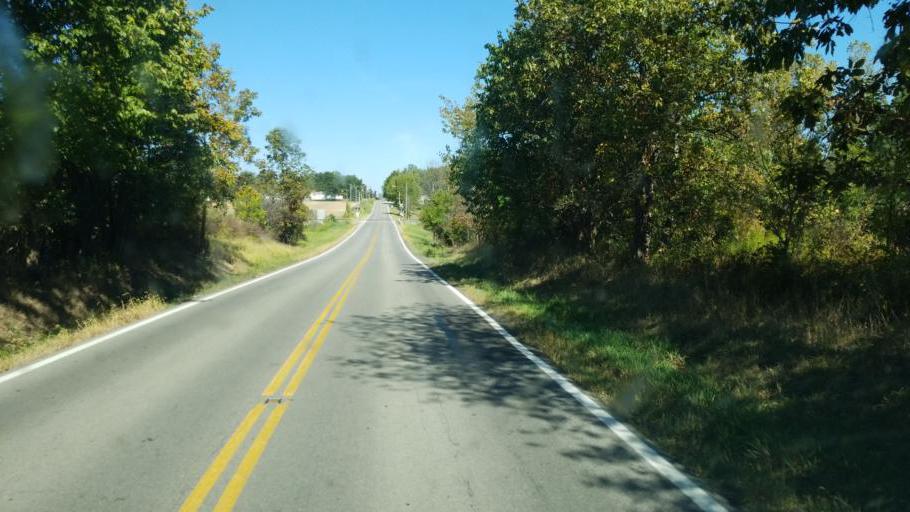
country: US
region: Ohio
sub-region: Huron County
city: Plymouth
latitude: 40.9870
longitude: -82.7063
